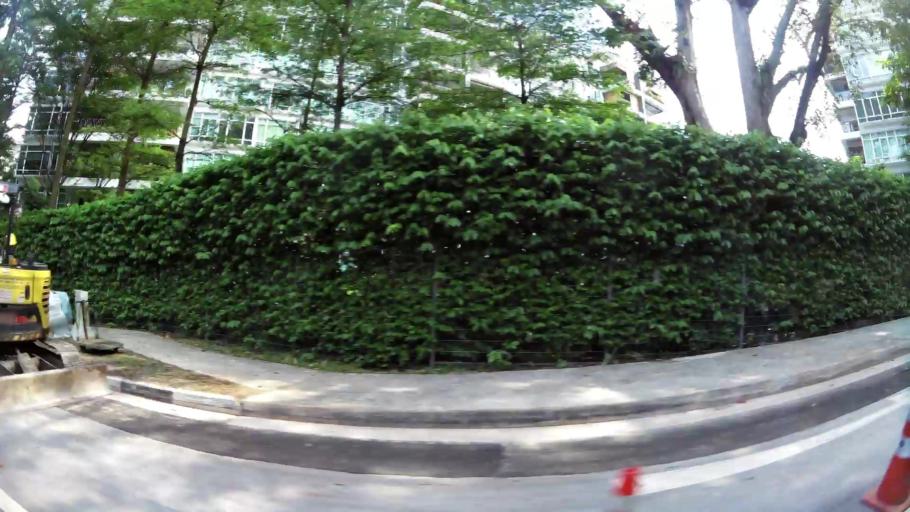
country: SG
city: Singapore
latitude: 1.2706
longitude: 103.8241
